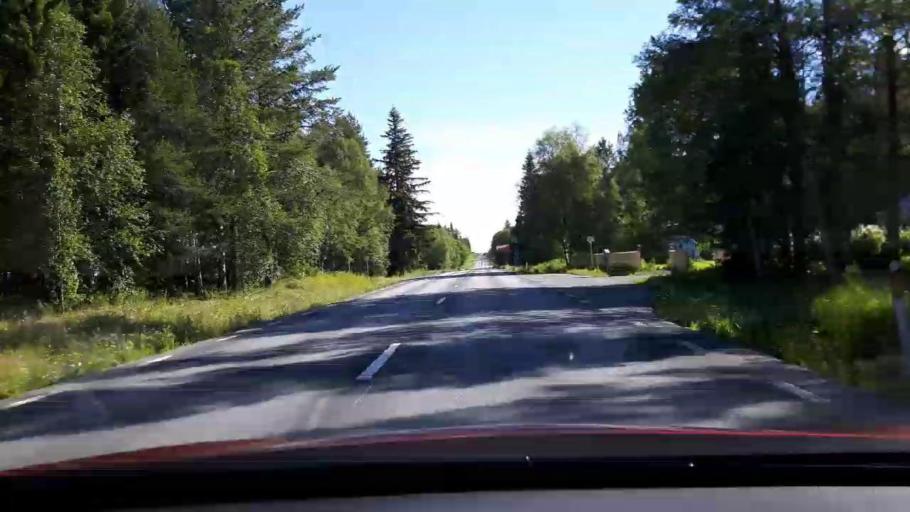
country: SE
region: Jaemtland
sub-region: OEstersunds Kommun
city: Lit
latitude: 63.2286
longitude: 14.7537
